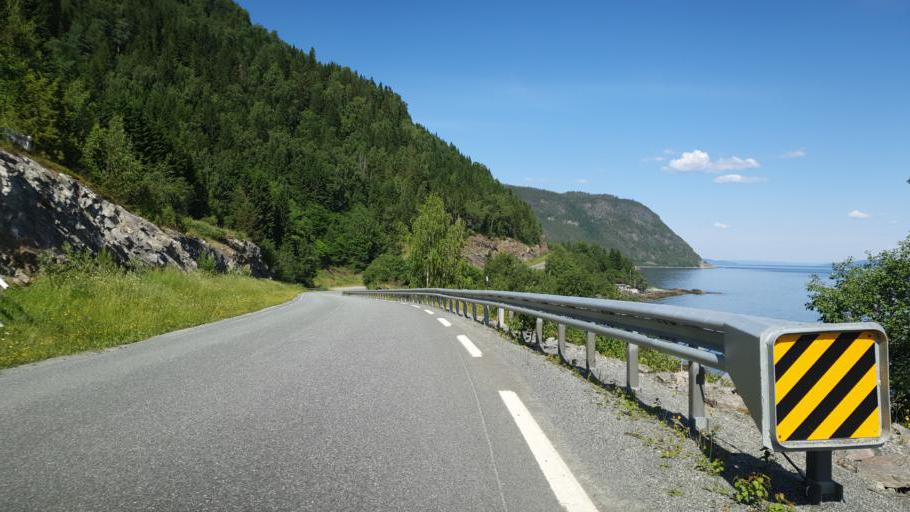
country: NO
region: Nord-Trondelag
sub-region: Leksvik
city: Leksvik
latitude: 63.6125
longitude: 10.5080
